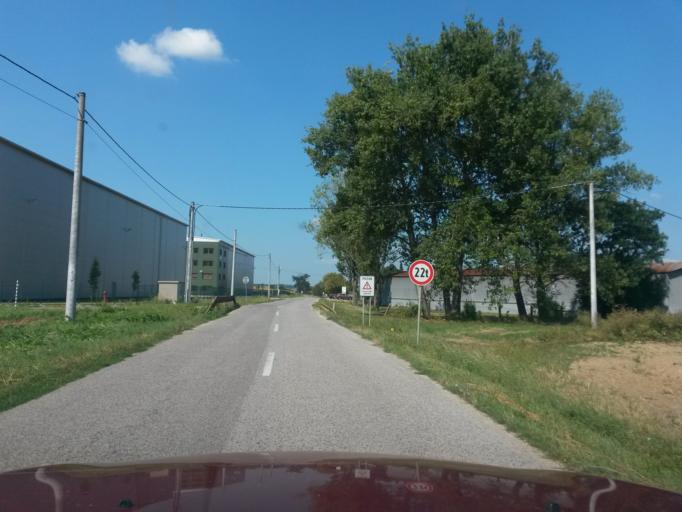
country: SK
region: Kosicky
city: Moldava nad Bodvou
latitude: 48.5335
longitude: 21.0911
